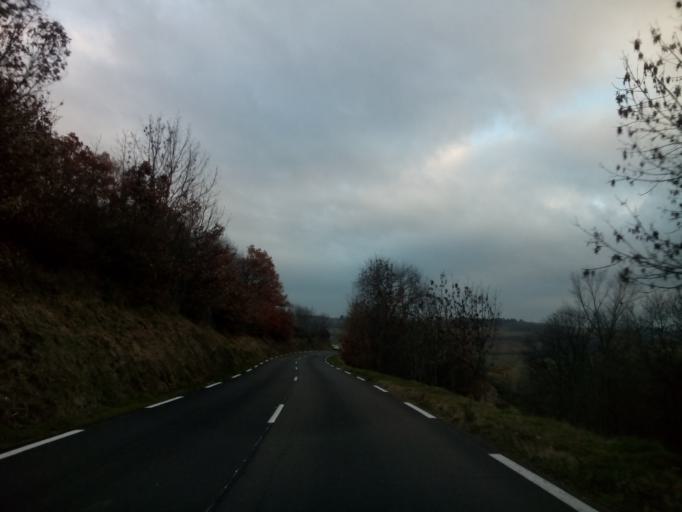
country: FR
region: Rhone-Alpes
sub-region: Departement de la Loire
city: Saint-Julien-Molin-Molette
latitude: 45.3263
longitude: 4.6275
